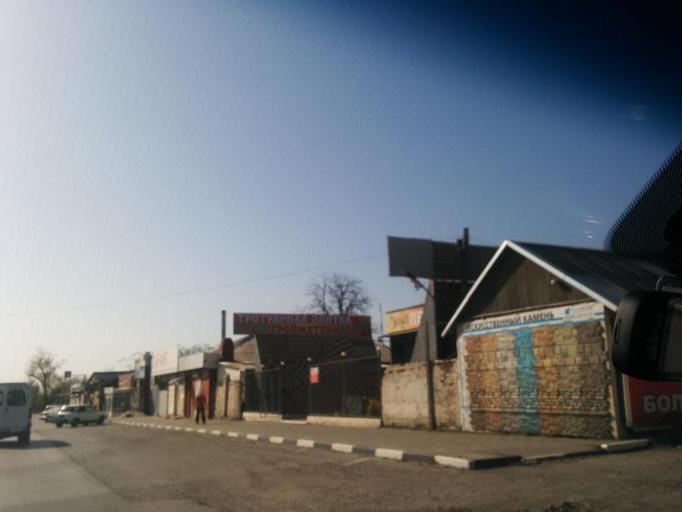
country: RU
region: Rostov
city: Mayskiy
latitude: 47.7121
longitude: 40.1418
